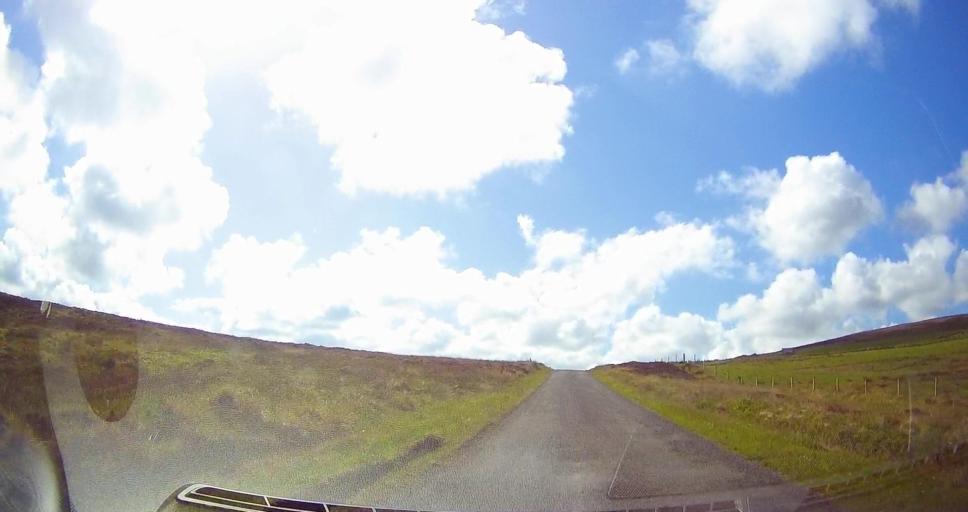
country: GB
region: Scotland
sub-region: Orkney Islands
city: Orkney
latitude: 59.0498
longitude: -3.1155
